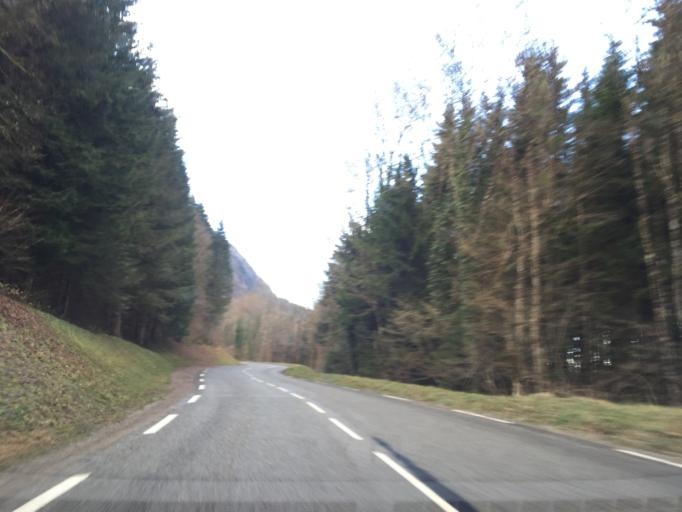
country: FR
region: Rhone-Alpes
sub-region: Departement de la Haute-Savoie
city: Gruffy
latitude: 45.7483
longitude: 6.0715
